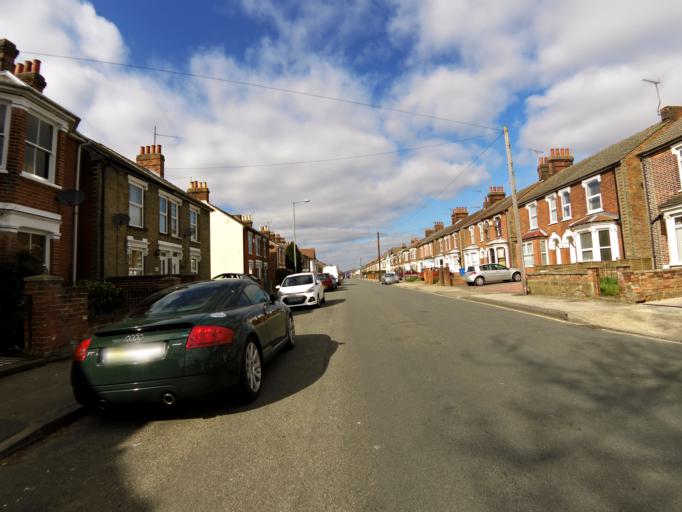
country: GB
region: England
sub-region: Suffolk
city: Ipswich
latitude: 52.0446
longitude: 1.1815
